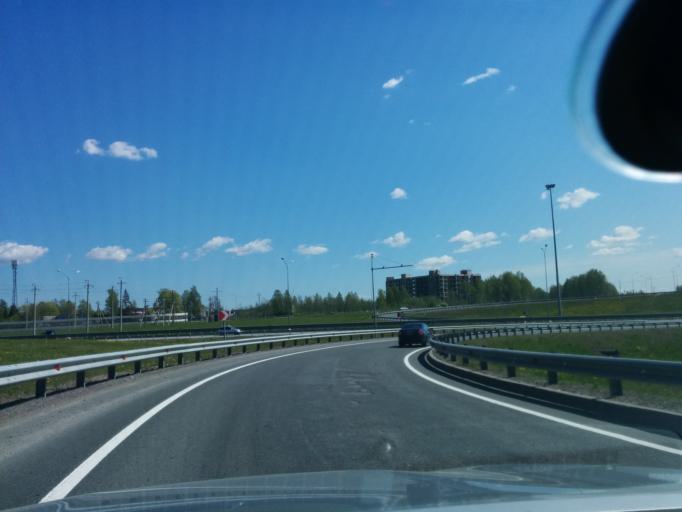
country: RU
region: Leningrad
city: Luppolovo
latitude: 60.1766
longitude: 30.3555
